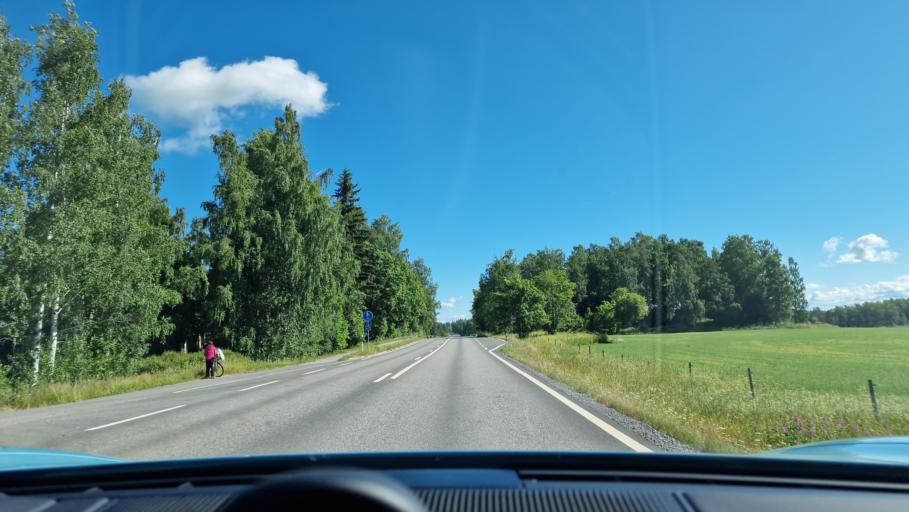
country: FI
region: Pirkanmaa
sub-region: Tampere
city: Kangasala
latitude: 61.4757
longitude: 24.1396
